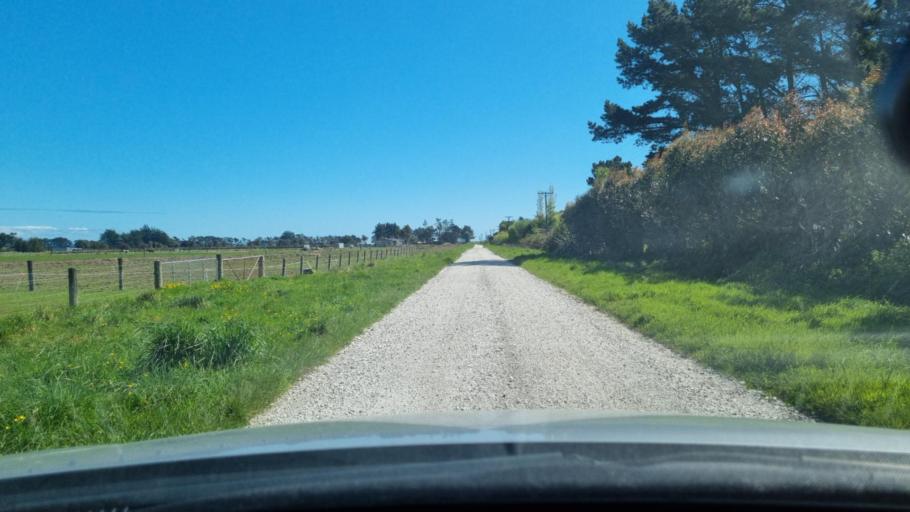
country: NZ
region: Southland
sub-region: Invercargill City
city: Invercargill
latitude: -46.3904
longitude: 168.3005
